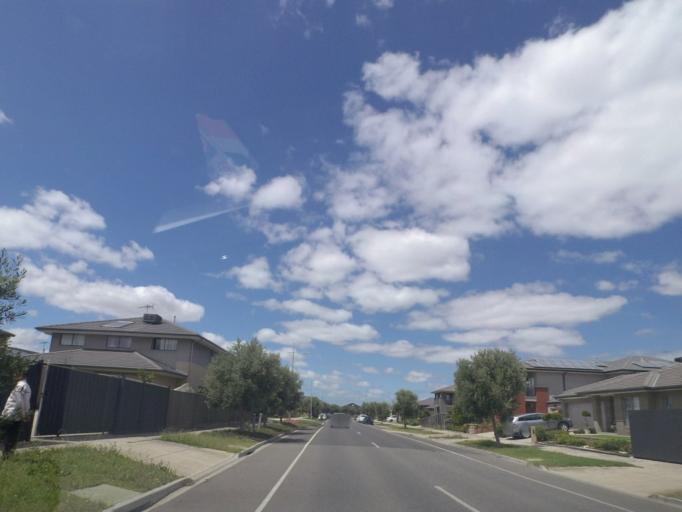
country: AU
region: Victoria
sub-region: Whittlesea
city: Lalor
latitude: -37.6636
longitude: 144.9967
